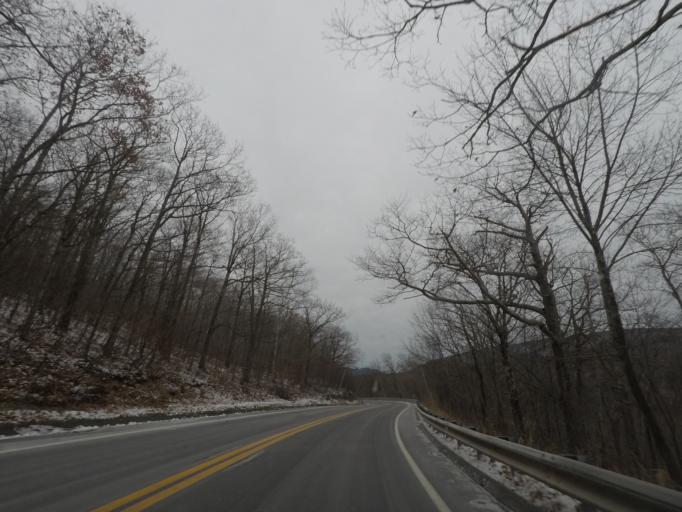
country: US
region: Massachusetts
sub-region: Berkshire County
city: Williamstown
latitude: 42.7156
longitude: -73.2606
